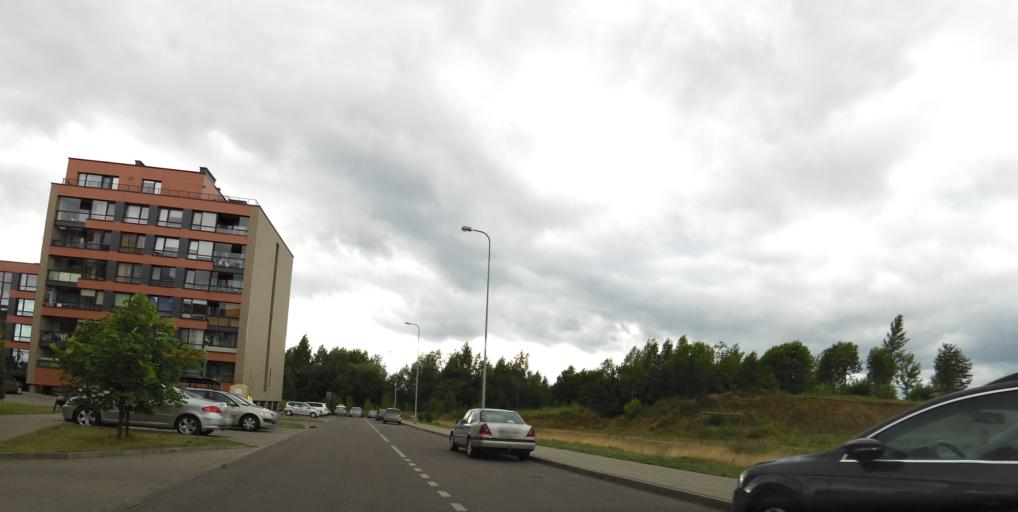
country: LT
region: Vilnius County
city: Pilaite
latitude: 54.7127
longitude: 25.1797
